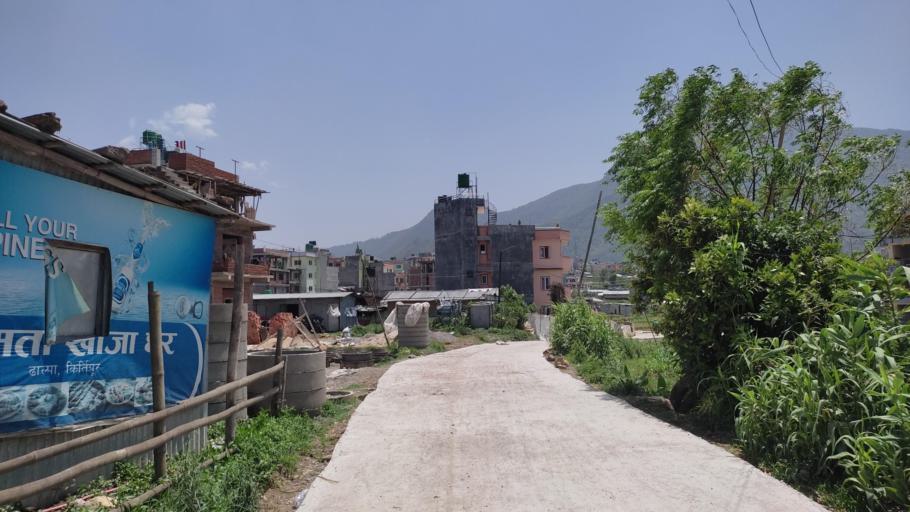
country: NP
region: Central Region
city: Kirtipur
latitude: 27.6748
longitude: 85.2697
